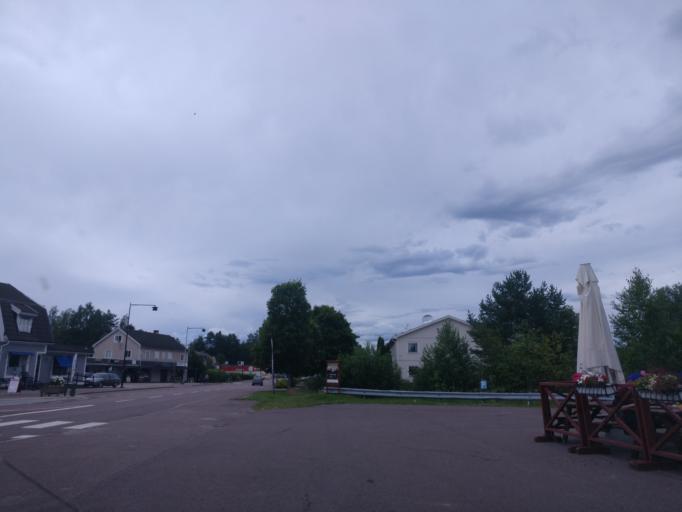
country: SE
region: Vaermland
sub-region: Hagfors Kommun
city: Ekshaerad
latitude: 60.1742
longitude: 13.4962
